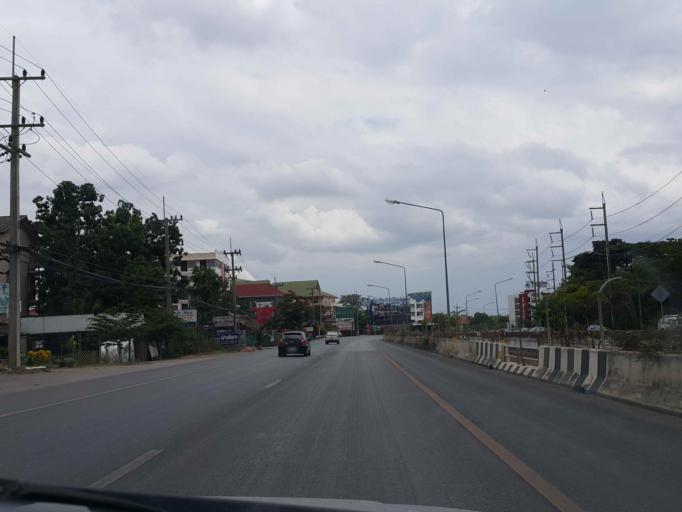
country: TH
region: Chiang Mai
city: Chiang Mai
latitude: 18.7812
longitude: 98.9584
